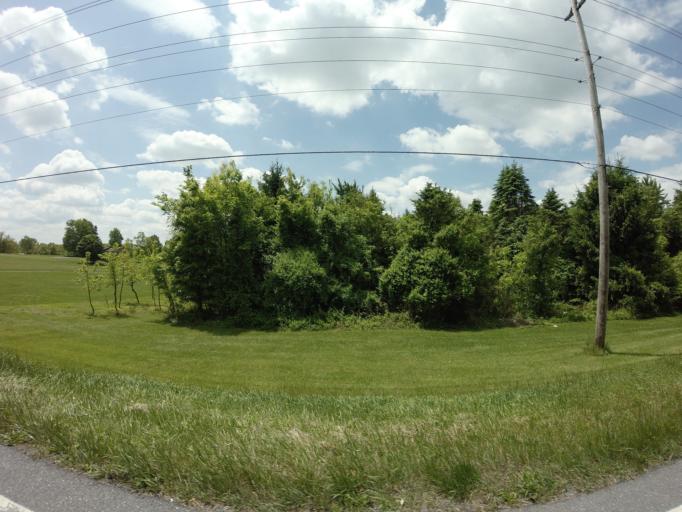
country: US
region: Maryland
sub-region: Frederick County
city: Green Valley
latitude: 39.3060
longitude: -77.3222
